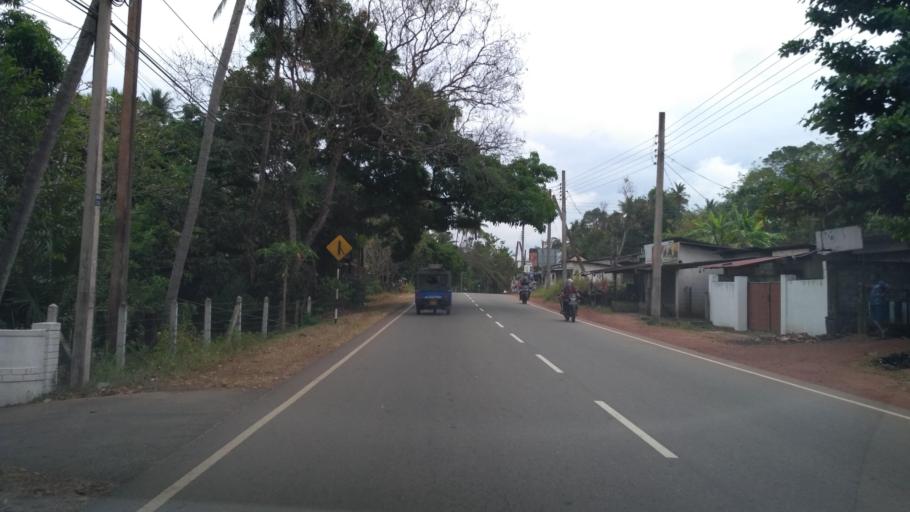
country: LK
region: North Western
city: Kuliyapitiya
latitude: 7.3272
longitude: 80.0503
